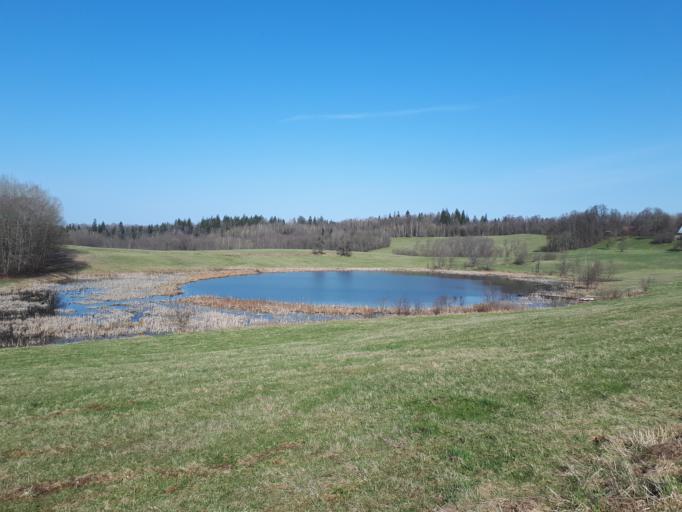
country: LT
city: Aukstadvaris
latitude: 54.5858
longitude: 24.6122
